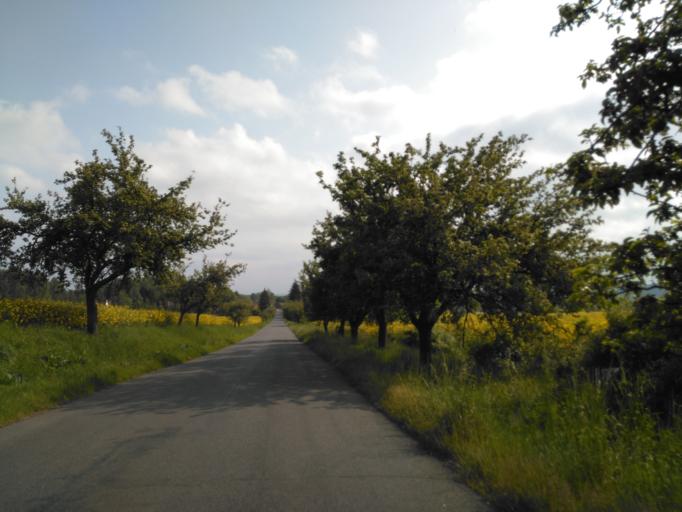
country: CZ
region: Plzensky
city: Zbiroh
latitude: 49.8752
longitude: 13.7974
